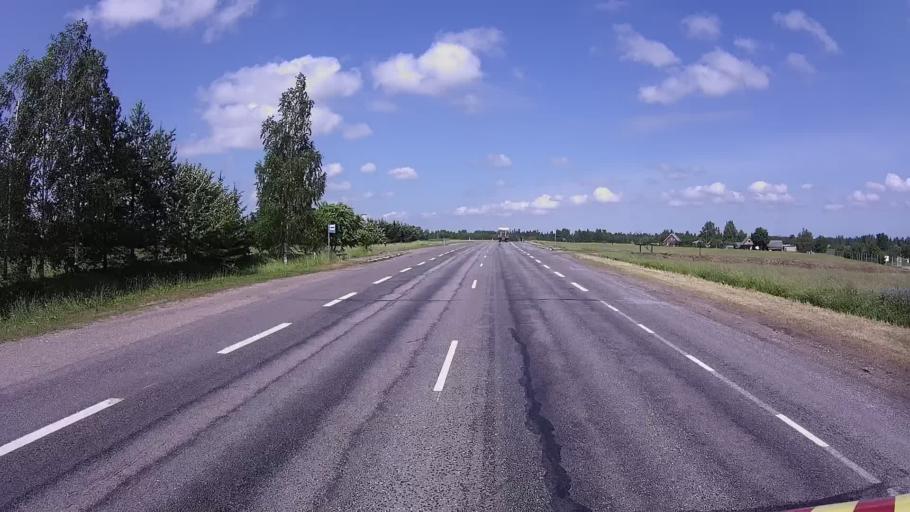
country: EE
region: Tartu
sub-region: UElenurme vald
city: Ulenurme
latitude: 58.2759
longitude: 26.7356
